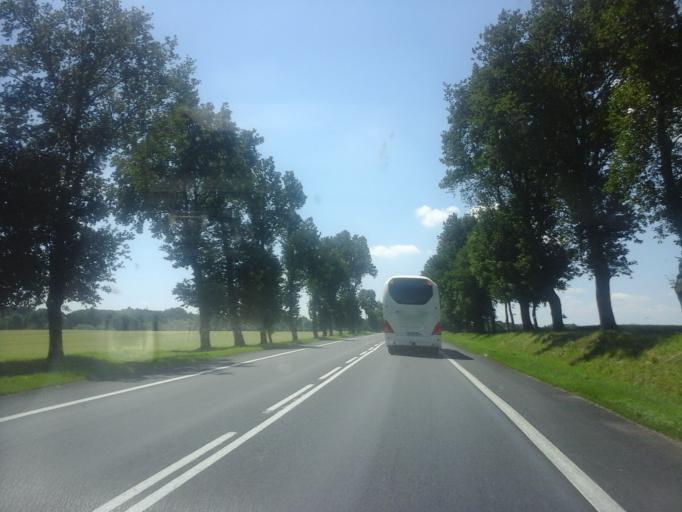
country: PL
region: West Pomeranian Voivodeship
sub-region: Powiat bialogardzki
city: Bialogard
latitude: 54.1148
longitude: 16.0040
